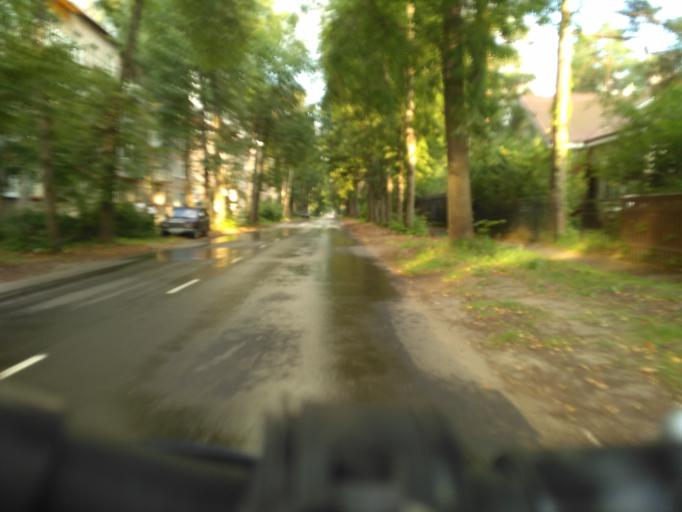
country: RU
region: Moskovskaya
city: Dubna
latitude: 56.7495
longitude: 37.1917
